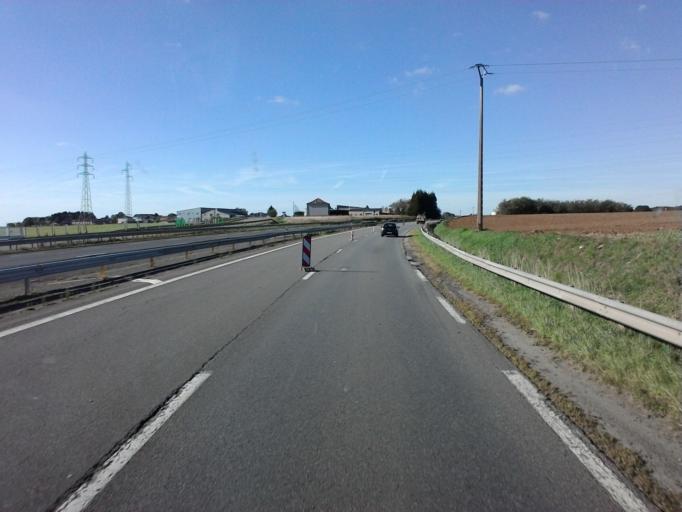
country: FR
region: Lorraine
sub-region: Departement de Meurthe-et-Moselle
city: Villers-la-Montagne
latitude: 49.4831
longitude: 5.8165
